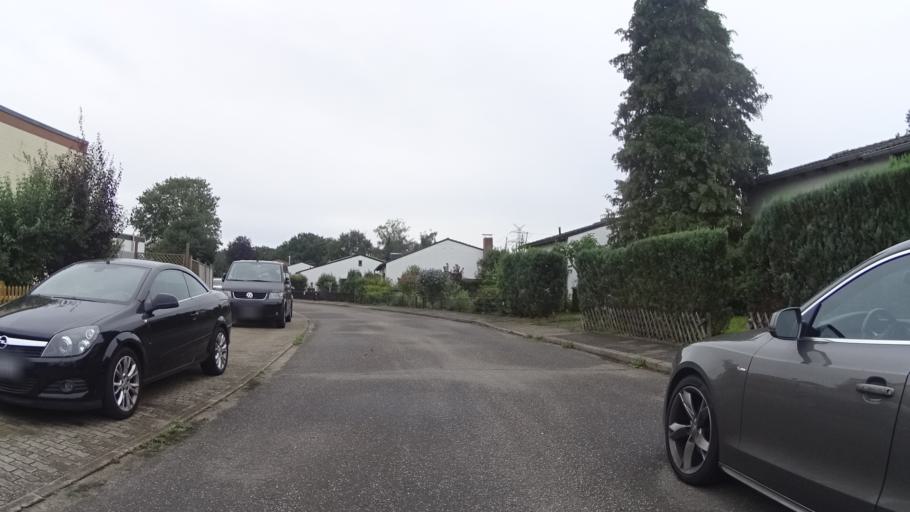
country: DE
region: Schleswig-Holstein
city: Henstedt-Ulzburg
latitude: 53.7702
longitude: 9.9723
